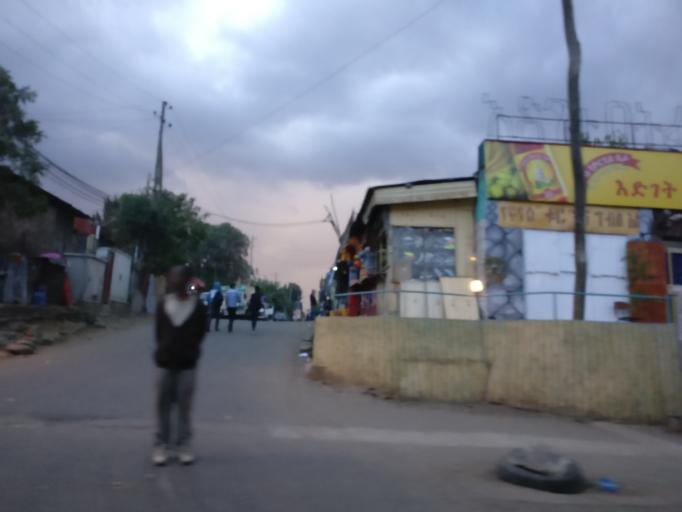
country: ET
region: Adis Abeba
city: Addis Ababa
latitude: 9.0139
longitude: 38.7344
